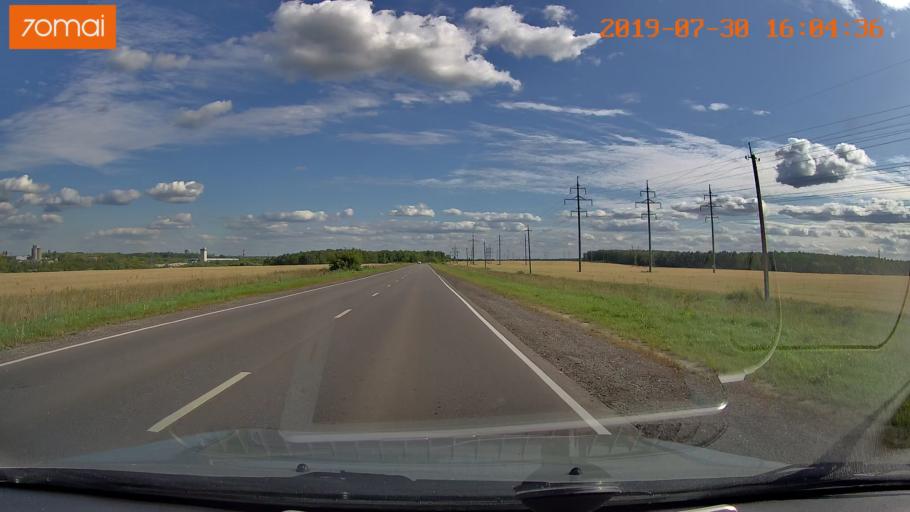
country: RU
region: Moskovskaya
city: Lopatinskiy
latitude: 55.2787
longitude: 38.7088
